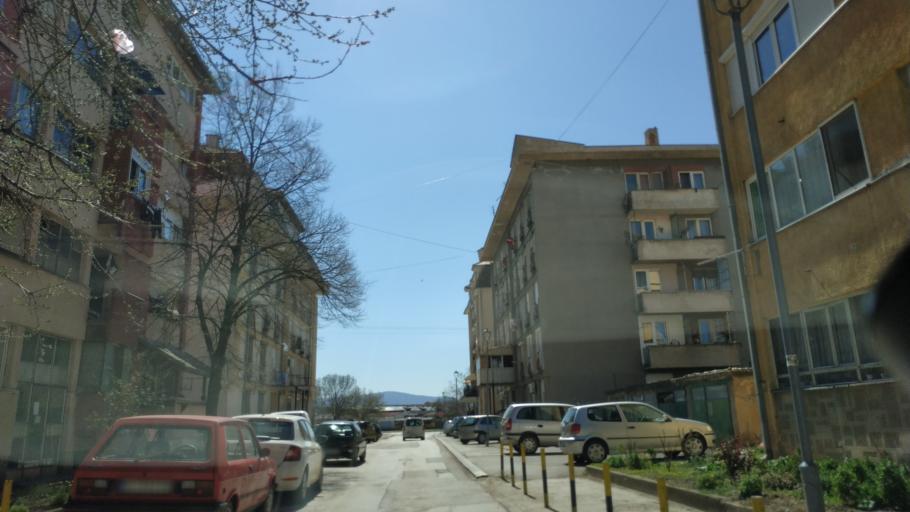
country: RS
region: Central Serbia
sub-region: Nisavski Okrug
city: Aleksinac
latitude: 43.5374
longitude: 21.7071
